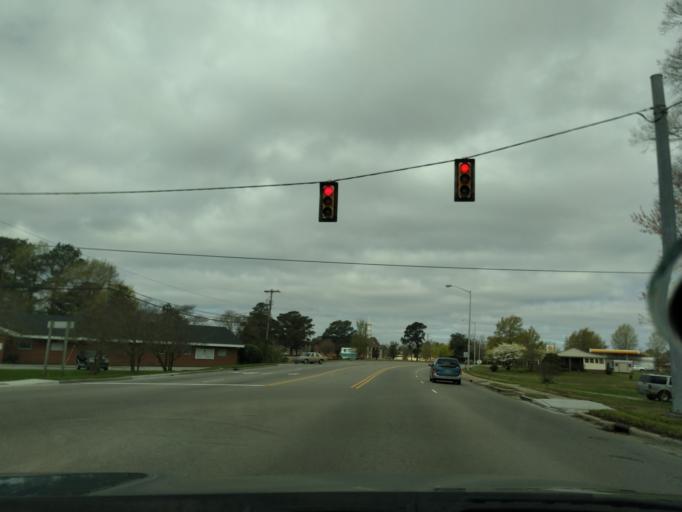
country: US
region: North Carolina
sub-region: Chowan County
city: Edenton
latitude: 36.0706
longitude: -76.6081
